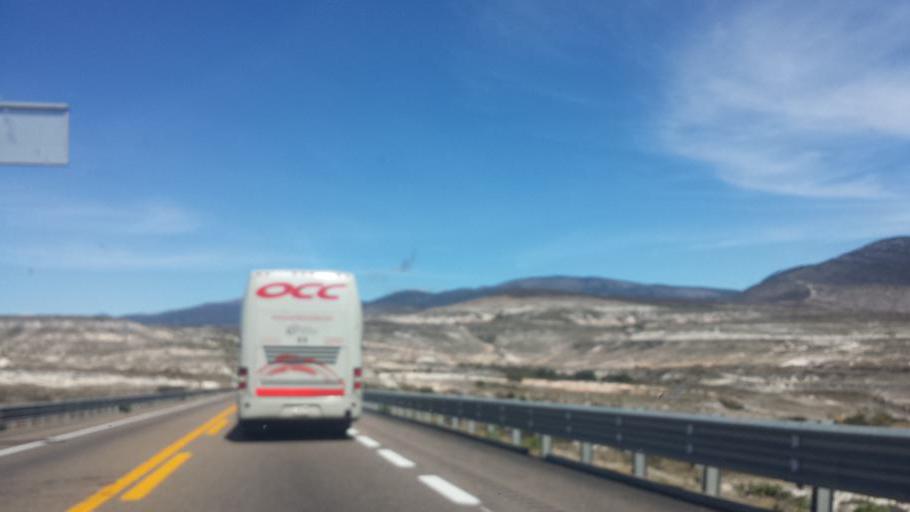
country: MX
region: Oaxaca
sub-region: Villa Tejupam de la Union
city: Villa Tejupam de la Union
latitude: 17.8960
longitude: -97.3693
